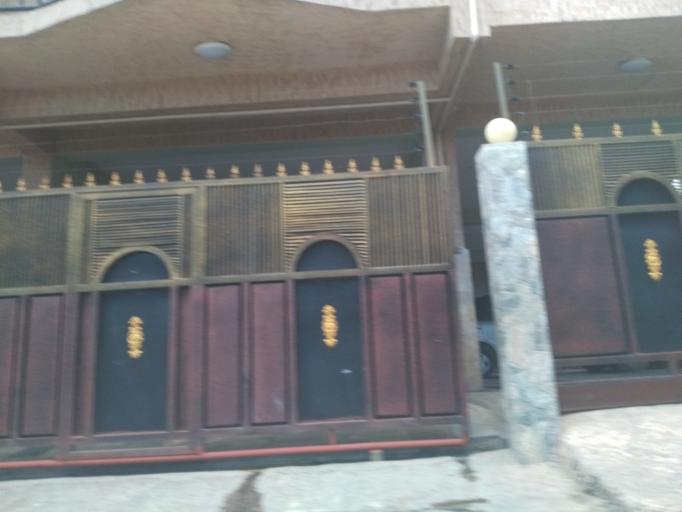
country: TZ
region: Dar es Salaam
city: Magomeni
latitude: -6.7914
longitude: 39.2689
